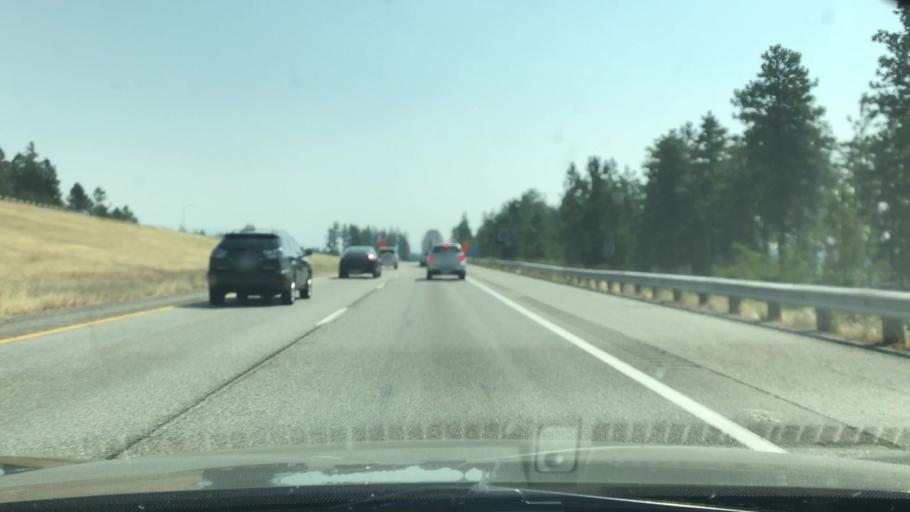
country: US
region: Idaho
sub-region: Kootenai County
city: Post Falls
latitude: 47.7088
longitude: -116.8799
